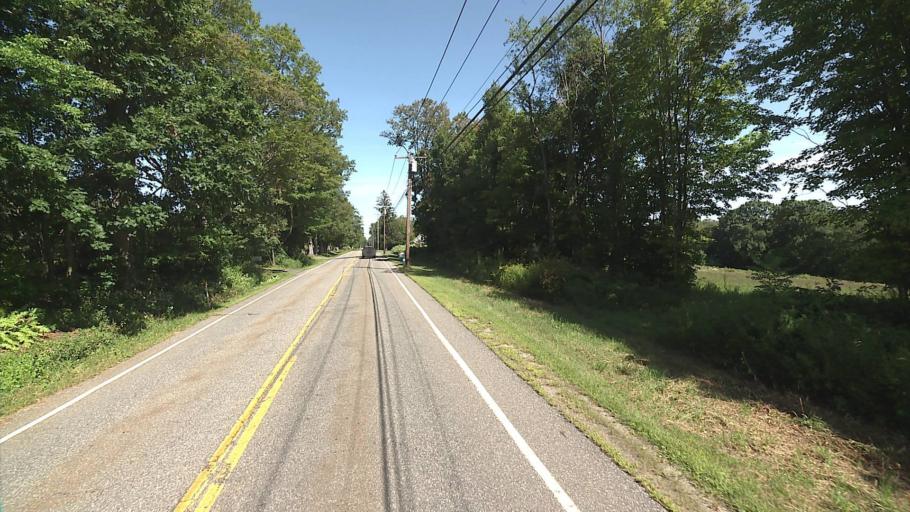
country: US
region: Connecticut
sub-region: Litchfield County
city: Northwest Harwinton
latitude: 41.7555
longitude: -73.0825
